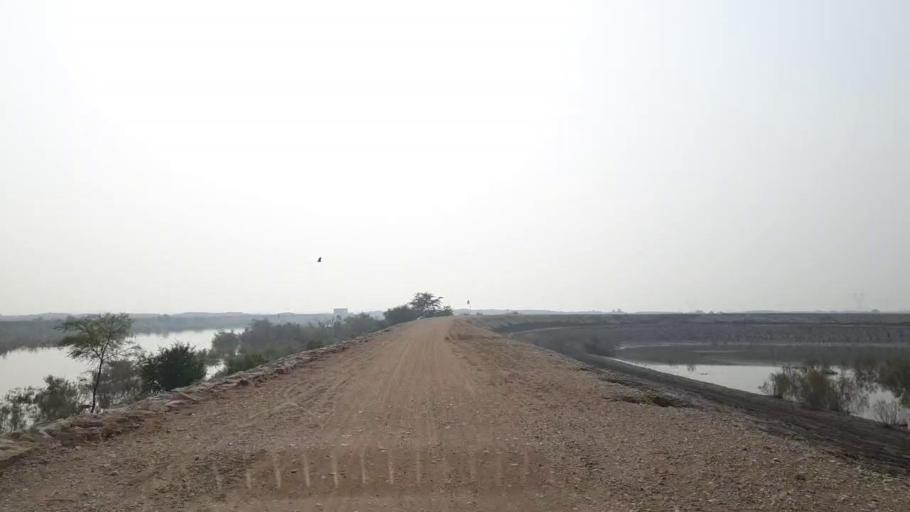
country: PK
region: Sindh
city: Sehwan
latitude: 26.4005
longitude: 67.8309
